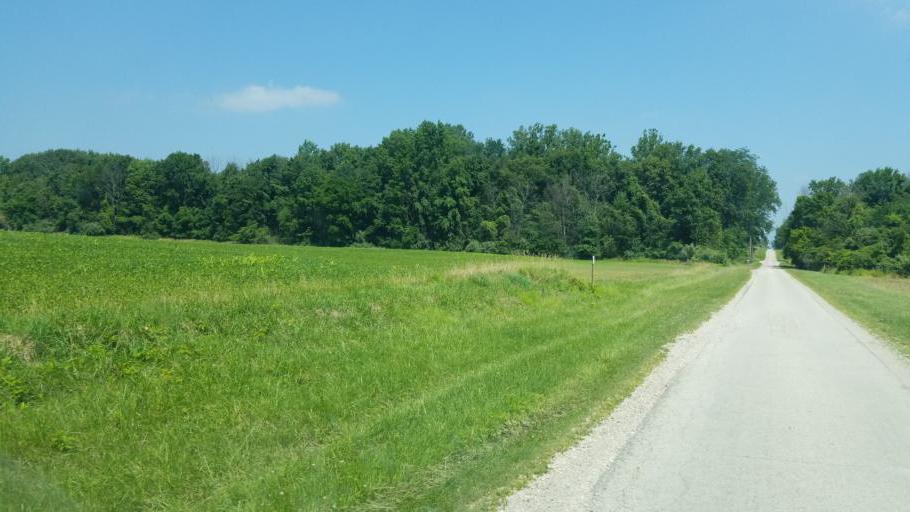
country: US
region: Ohio
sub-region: Seneca County
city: Tiffin
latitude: 41.0522
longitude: -82.9771
